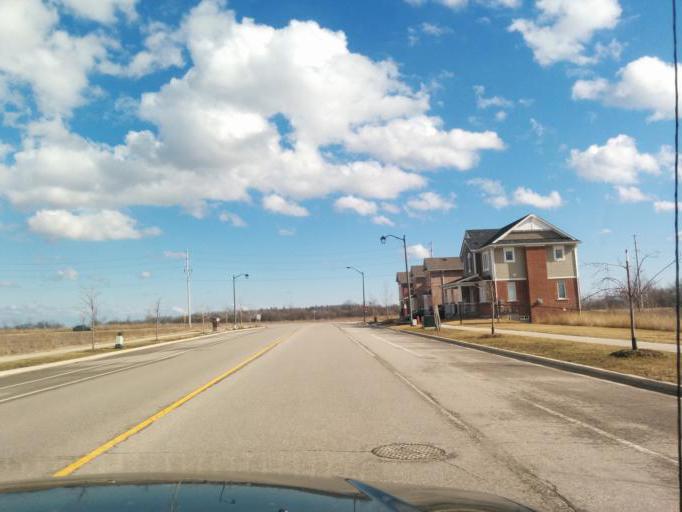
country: CA
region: Ontario
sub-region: Halton
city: Milton
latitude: 43.5010
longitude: -79.8455
